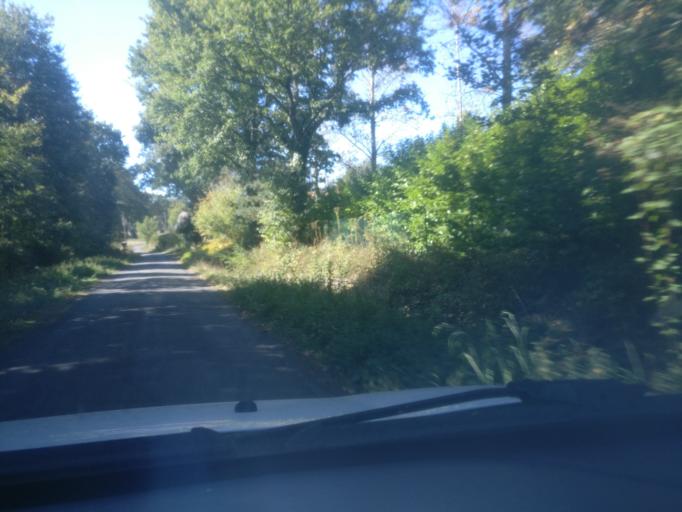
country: FR
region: Brittany
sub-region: Departement d'Ille-et-Vilaine
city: Saint-Thurial
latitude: 48.0564
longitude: -1.9111
